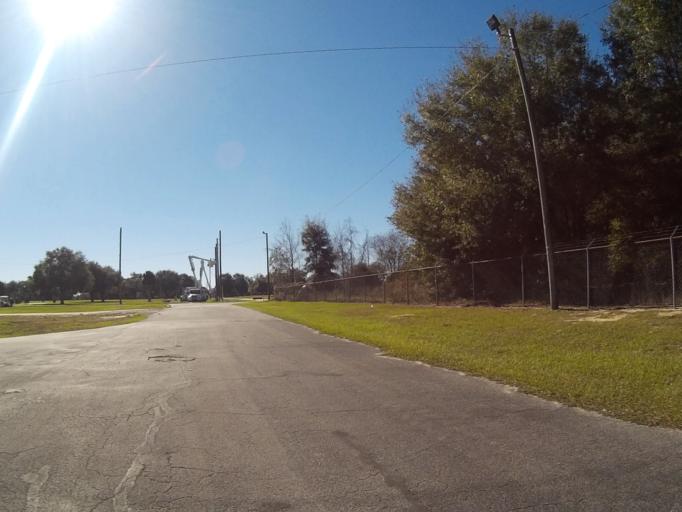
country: US
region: Florida
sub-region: Lake County
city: Umatilla
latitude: 28.9646
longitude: -81.6586
